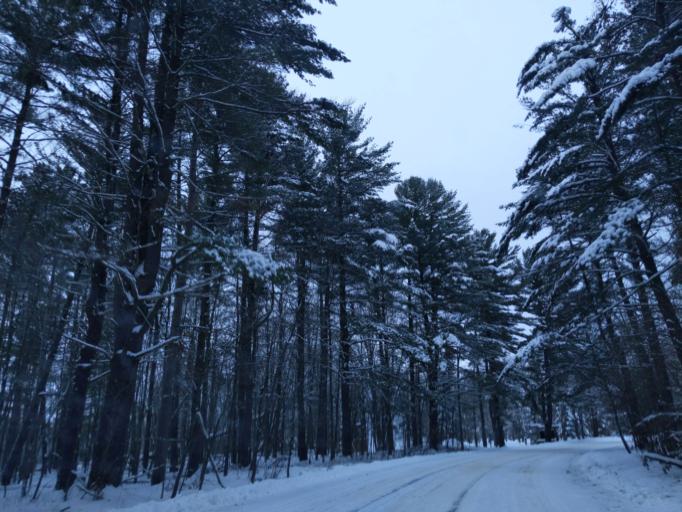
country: US
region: Wisconsin
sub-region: Marathon County
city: Marathon
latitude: 44.7710
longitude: -89.8691
